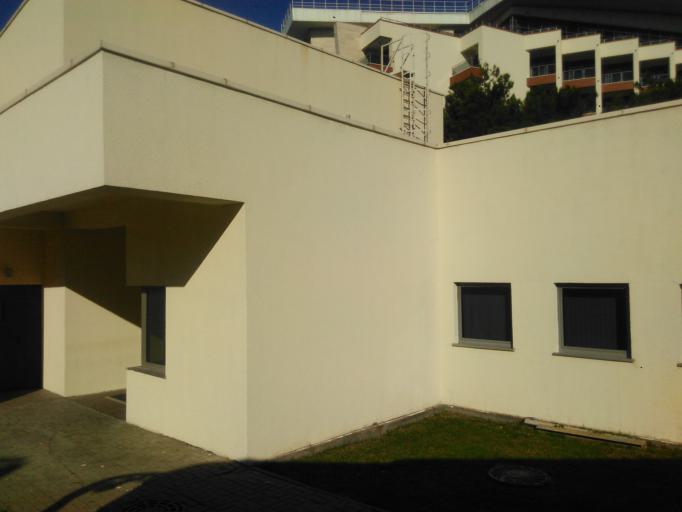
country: RU
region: Krasnodarskiy
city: Gelendzhik
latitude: 44.5505
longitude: 38.0544
